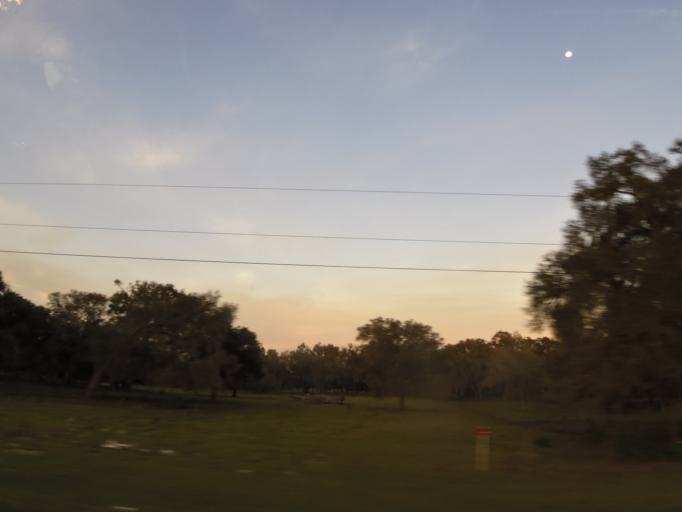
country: US
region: Florida
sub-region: Volusia County
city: De Leon Springs
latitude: 29.1485
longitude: -81.2889
